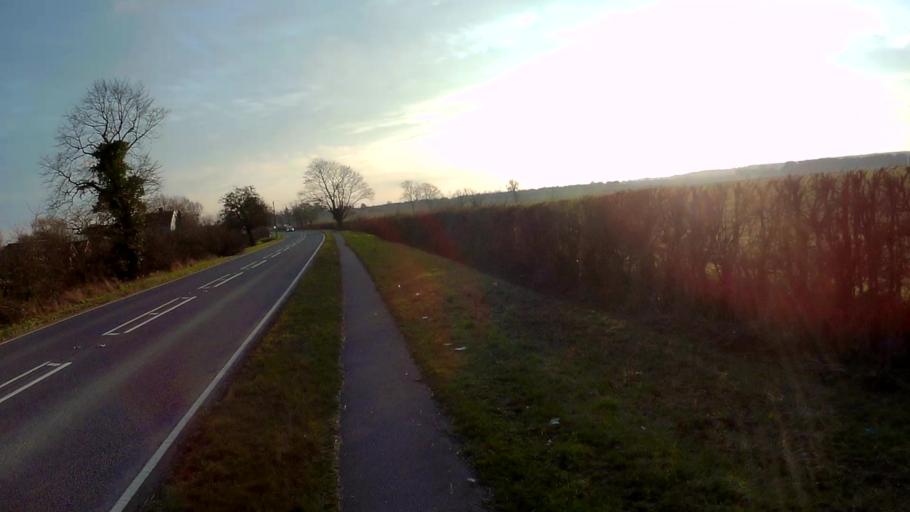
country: GB
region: England
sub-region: Lincolnshire
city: Bourne
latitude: 52.7847
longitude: -0.3773
